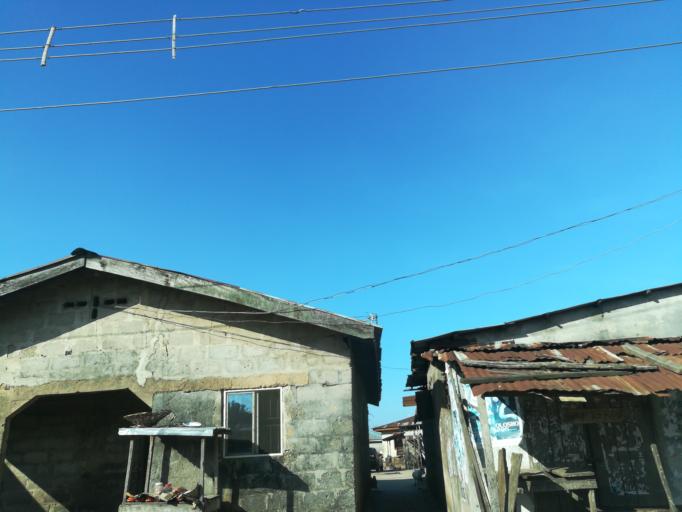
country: NG
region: Lagos
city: Ikorodu
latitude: 6.5377
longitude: 3.5525
